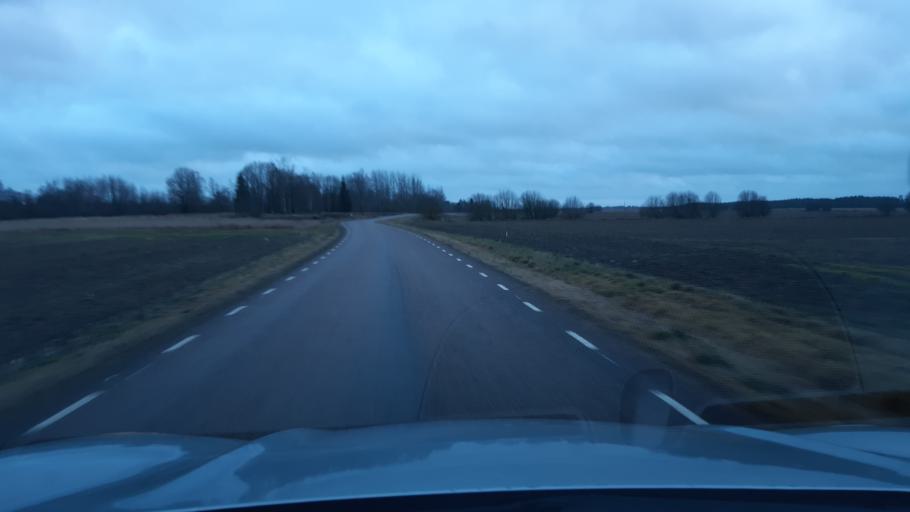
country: EE
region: Raplamaa
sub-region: Rapla vald
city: Rapla
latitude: 59.0076
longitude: 24.7103
